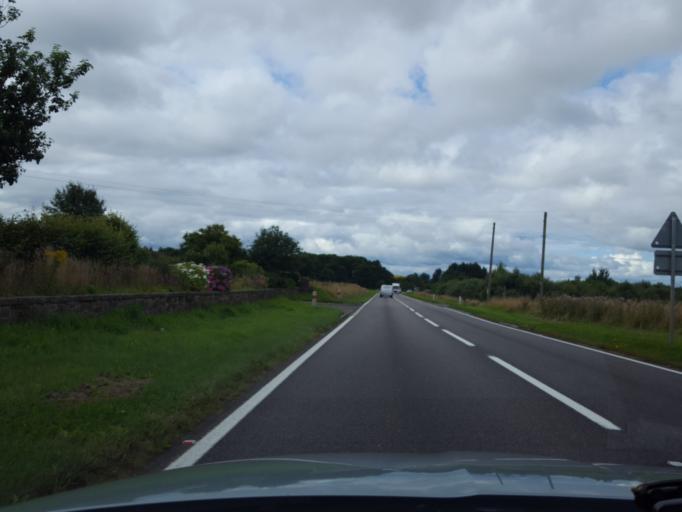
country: GB
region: Scotland
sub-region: Moray
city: Kinloss
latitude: 57.6282
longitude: -3.5148
